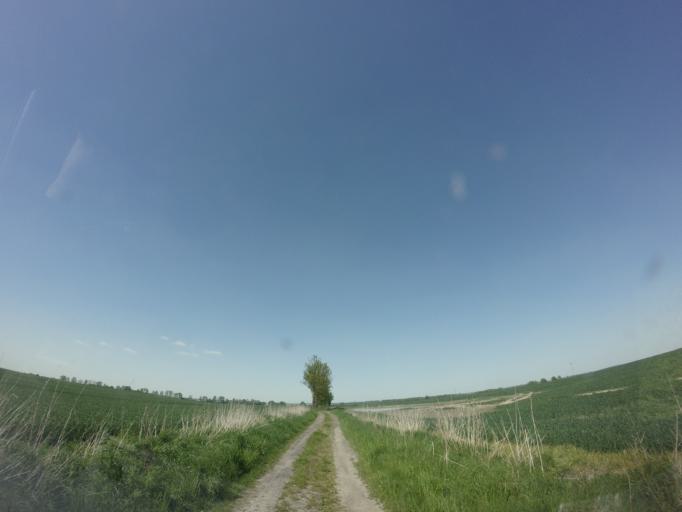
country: PL
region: West Pomeranian Voivodeship
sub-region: Powiat choszczenski
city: Pelczyce
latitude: 53.0555
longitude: 15.3825
